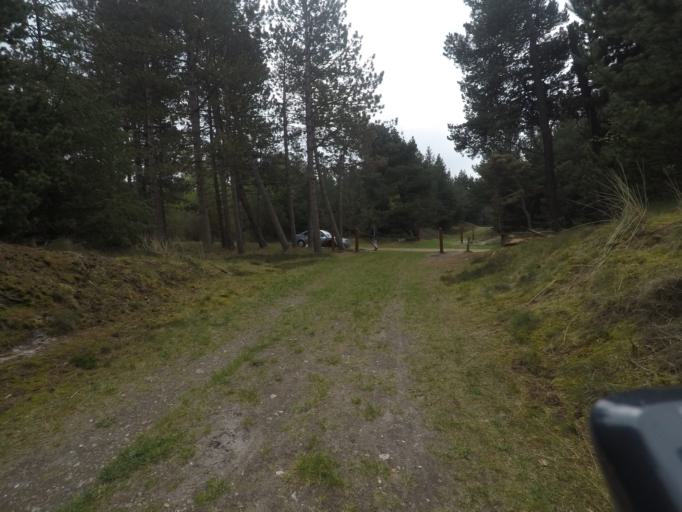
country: DE
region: Schleswig-Holstein
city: List
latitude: 55.1020
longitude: 8.5243
